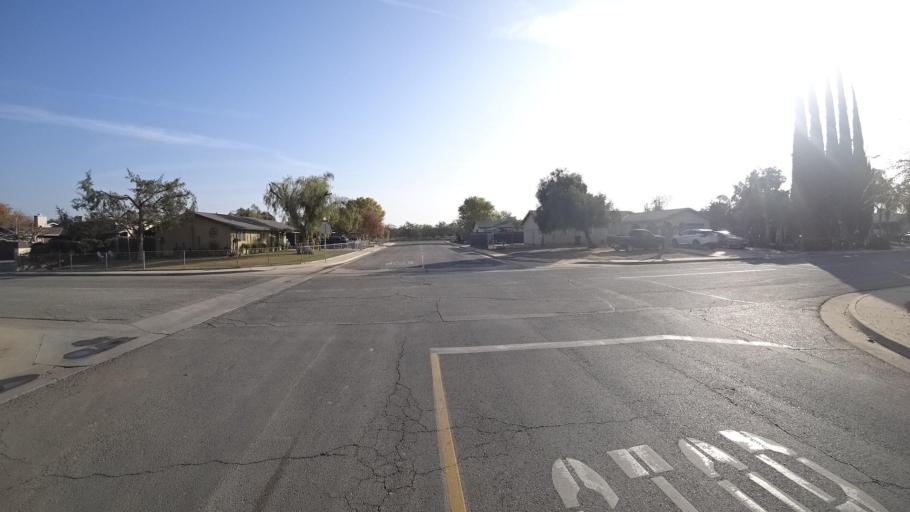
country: US
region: California
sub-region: Kern County
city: McFarland
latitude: 35.6799
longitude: -119.2186
